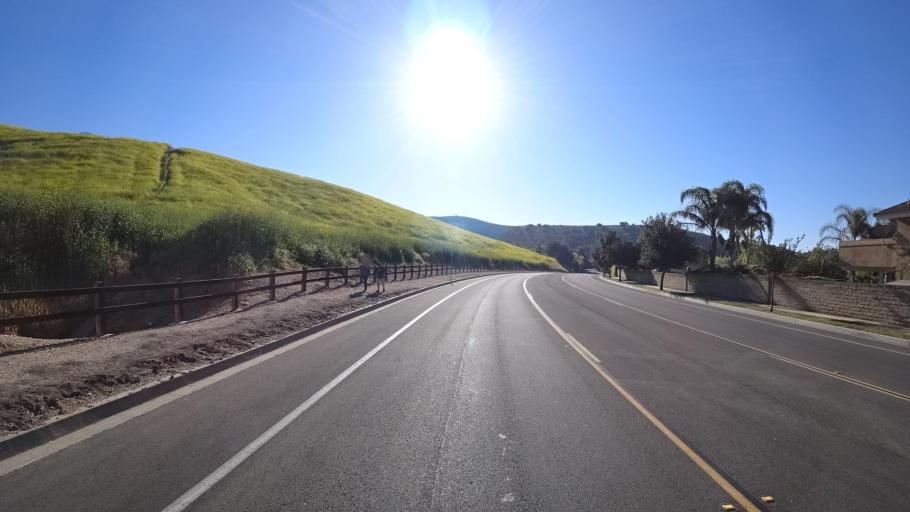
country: US
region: California
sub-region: Ventura County
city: Thousand Oaks
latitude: 34.1730
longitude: -118.8264
